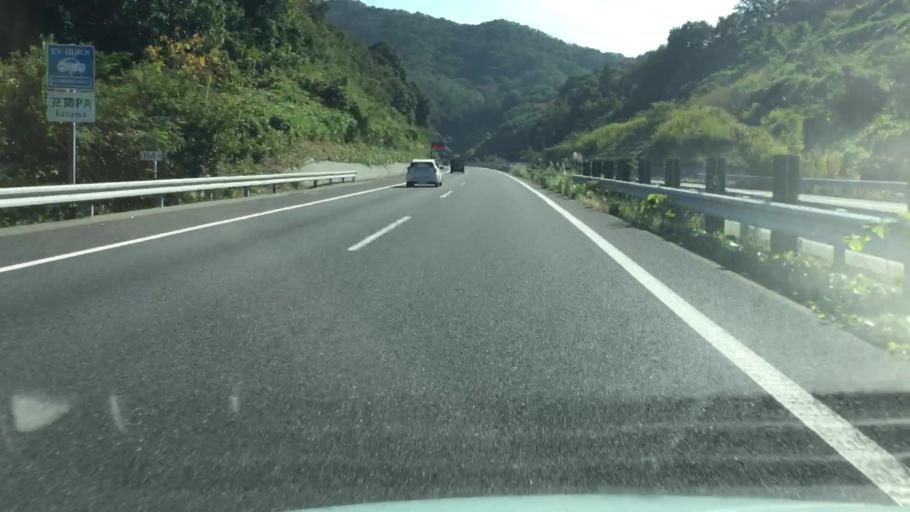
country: JP
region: Ibaraki
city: Kasama
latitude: 36.3401
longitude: 140.2269
